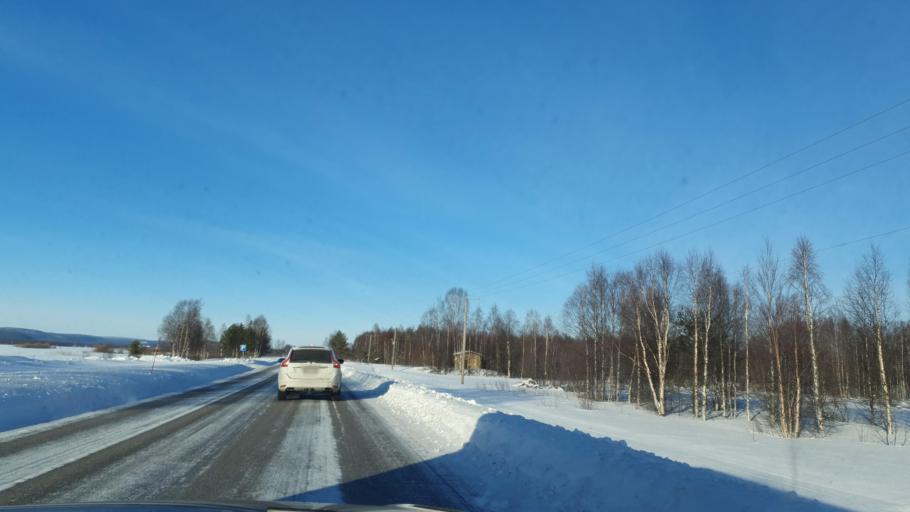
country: SE
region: Norrbotten
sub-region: Overtornea Kommun
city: OEvertornea
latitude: 66.3925
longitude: 23.6883
